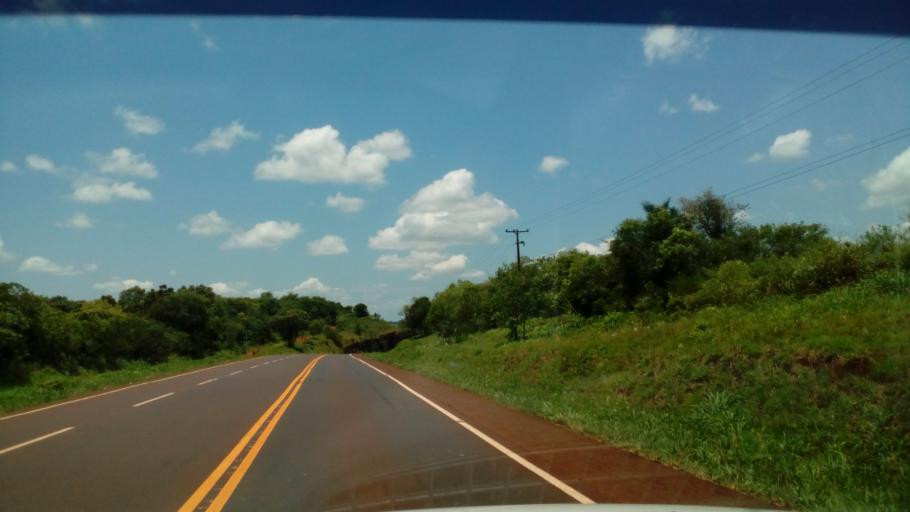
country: PY
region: Itapua
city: Arquitecto Tomas Romero Pereira
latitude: -26.4052
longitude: -55.2251
